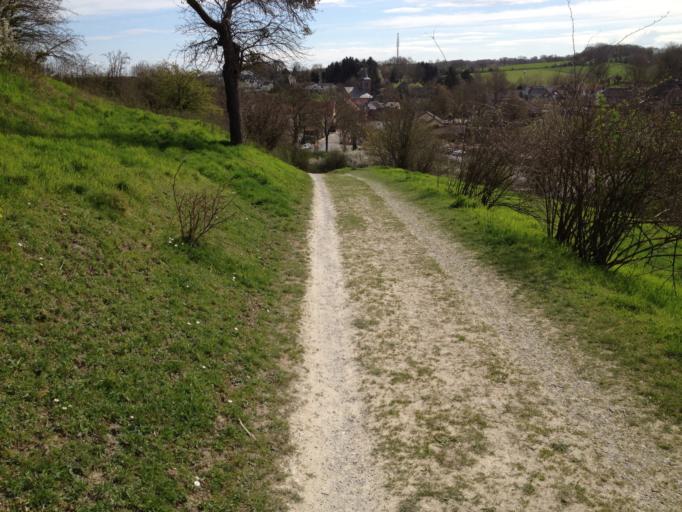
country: BE
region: Flanders
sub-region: Provincie Limburg
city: Sint-Pieters-Voeren
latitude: 50.7717
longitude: 5.8628
